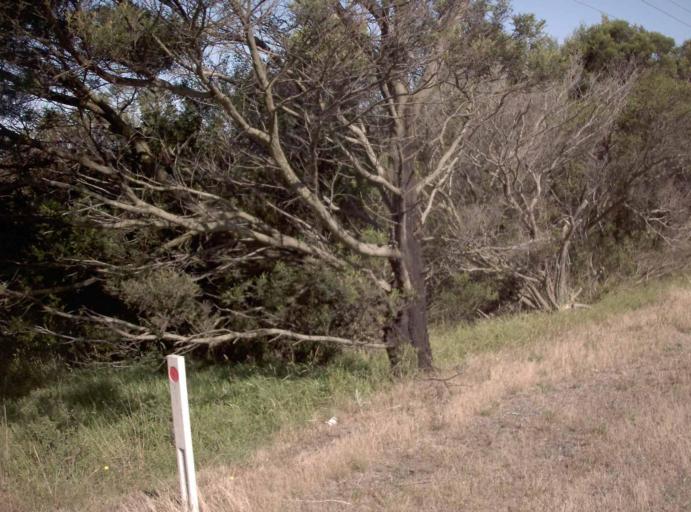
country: AU
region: Victoria
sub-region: Latrobe
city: Traralgon
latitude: -38.6218
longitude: 146.6728
